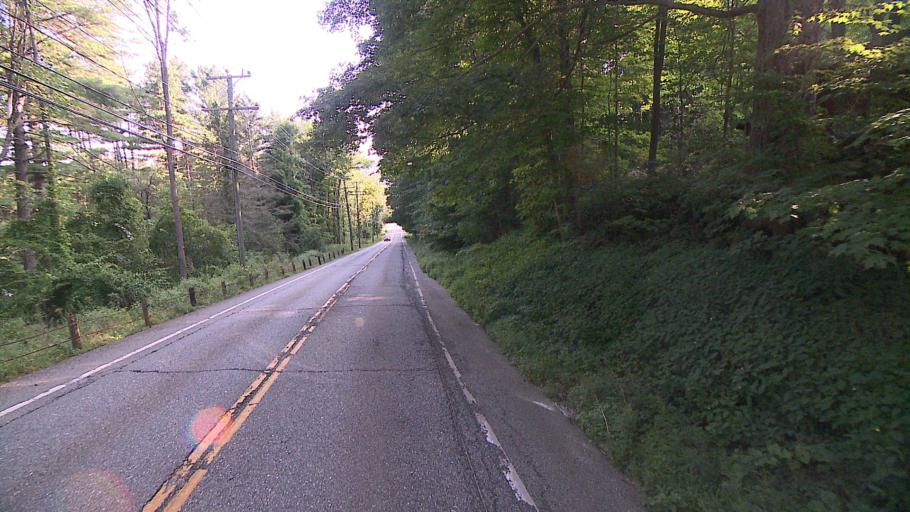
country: US
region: Connecticut
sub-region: Litchfield County
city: Kent
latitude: 41.8129
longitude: -73.3754
